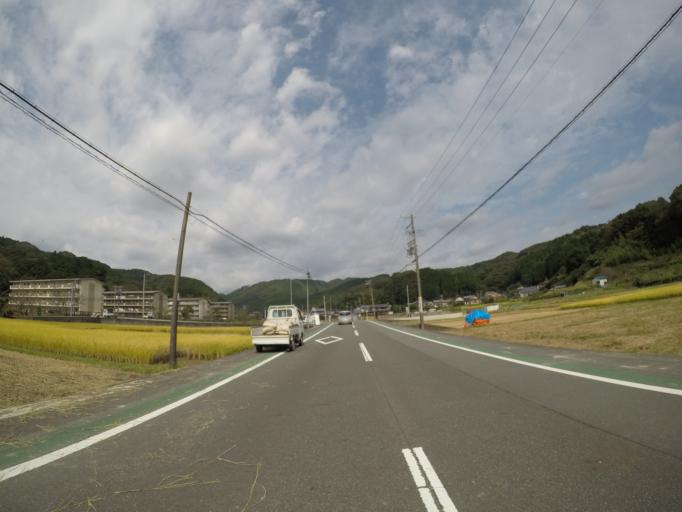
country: JP
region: Shizuoka
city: Shimada
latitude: 34.8642
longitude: 138.1832
